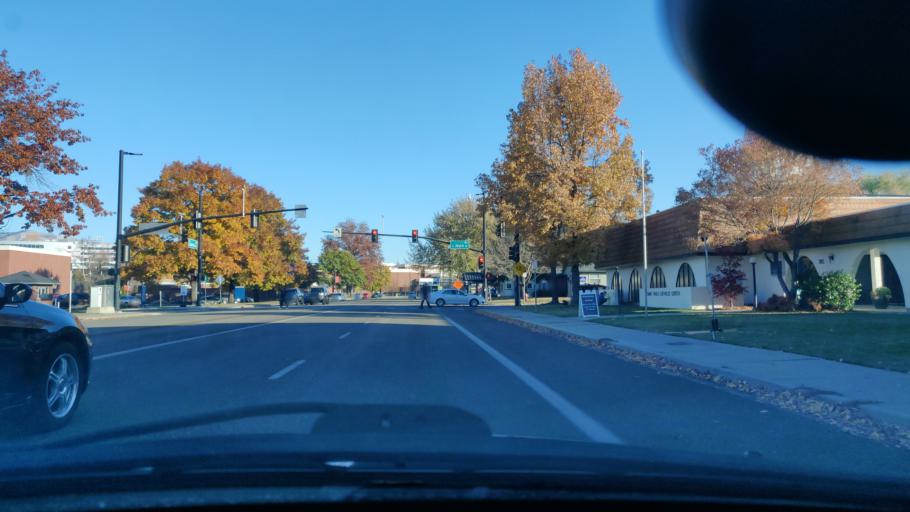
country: US
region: Idaho
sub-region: Ada County
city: Boise
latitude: 43.6031
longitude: -116.2052
